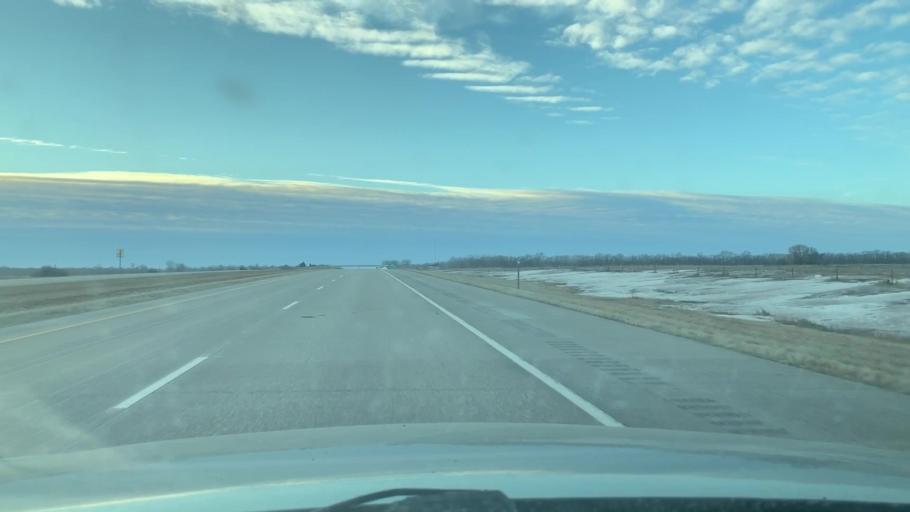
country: US
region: North Dakota
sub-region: Cass County
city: Casselton
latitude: 46.8749
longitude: -97.4189
